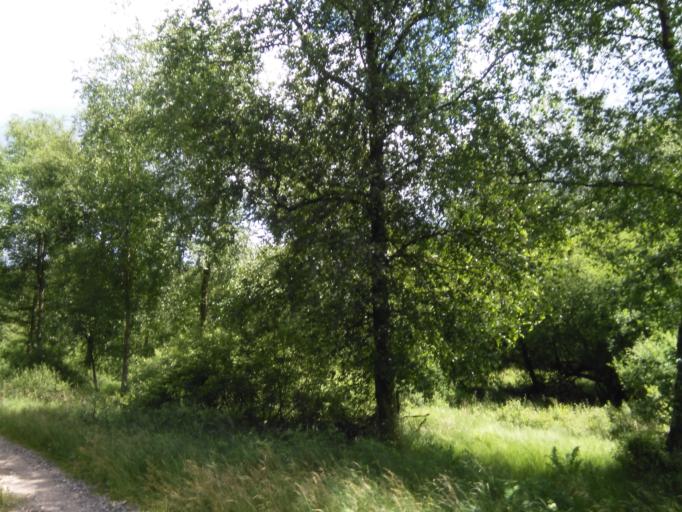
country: DK
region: Central Jutland
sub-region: Silkeborg Kommune
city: Virklund
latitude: 56.0686
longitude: 9.4500
